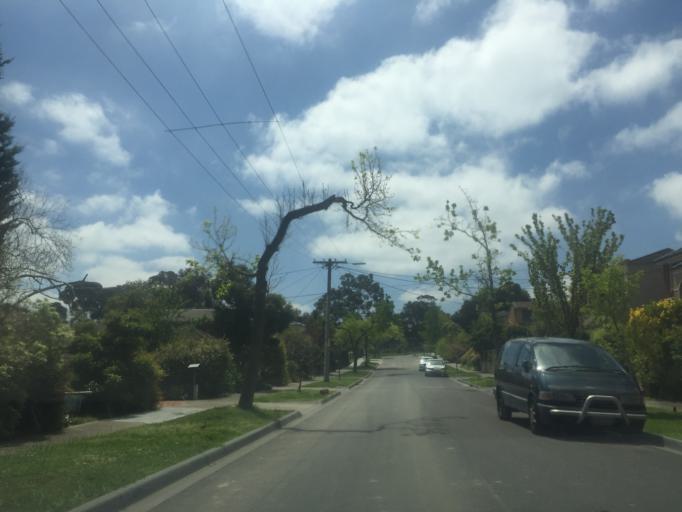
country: AU
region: Victoria
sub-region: Whitehorse
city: Mont Albert North
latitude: -37.8035
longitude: 145.0959
